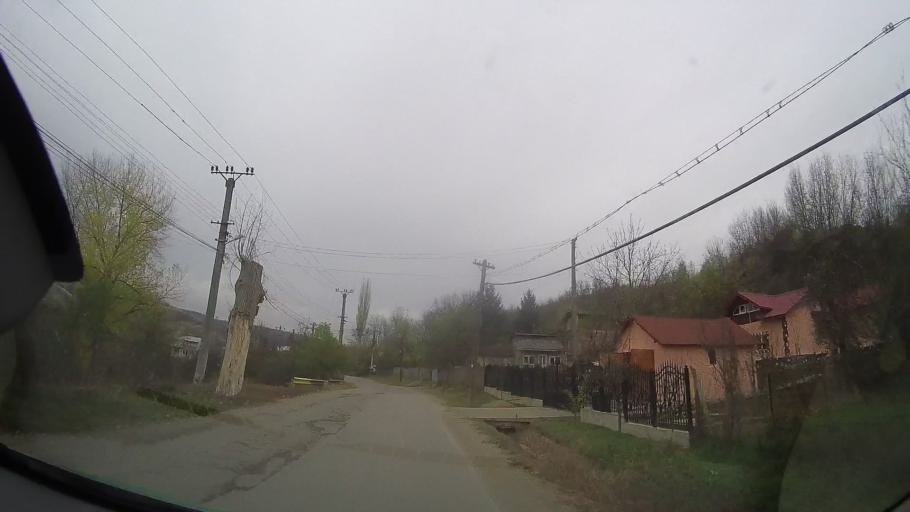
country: RO
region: Prahova
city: Ceptura de Sus
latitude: 45.0508
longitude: 26.2979
